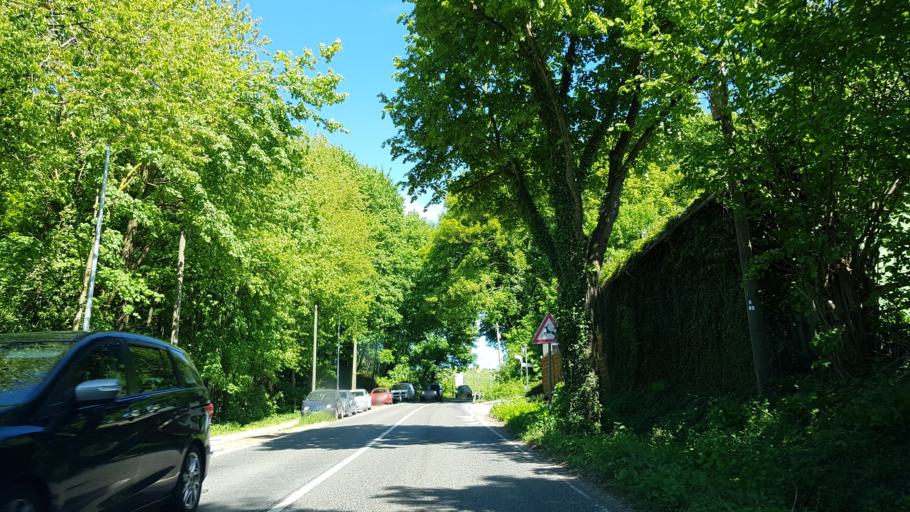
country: DE
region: North Rhine-Westphalia
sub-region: Regierungsbezirk Dusseldorf
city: Heiligenhaus
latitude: 51.3082
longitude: 6.9506
